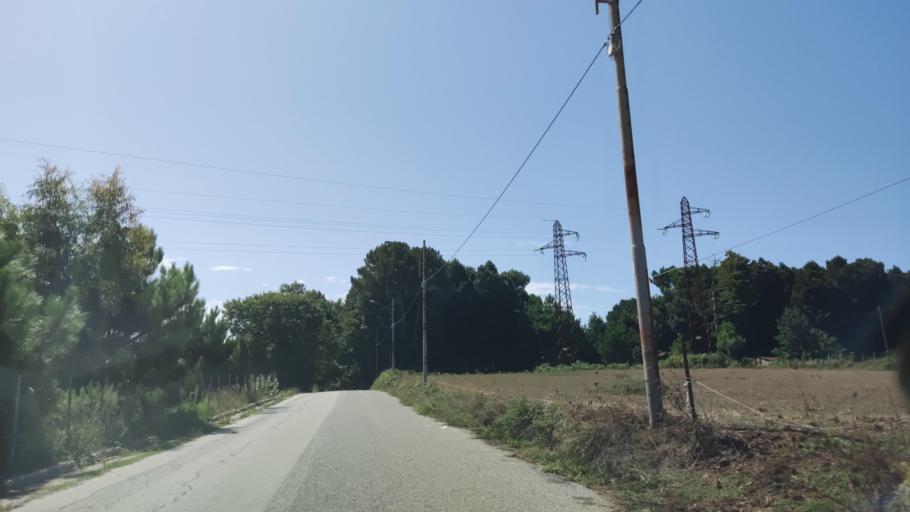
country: IT
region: Calabria
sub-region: Provincia di Reggio Calabria
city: Seminara
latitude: 38.3431
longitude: 15.8439
